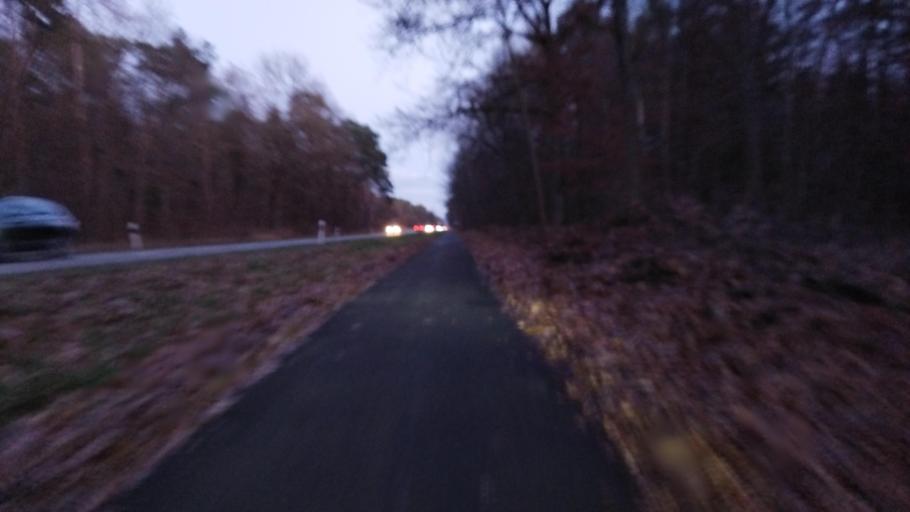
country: DE
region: Rheinland-Pfalz
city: Dudenhofen
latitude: 49.3451
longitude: 8.3843
